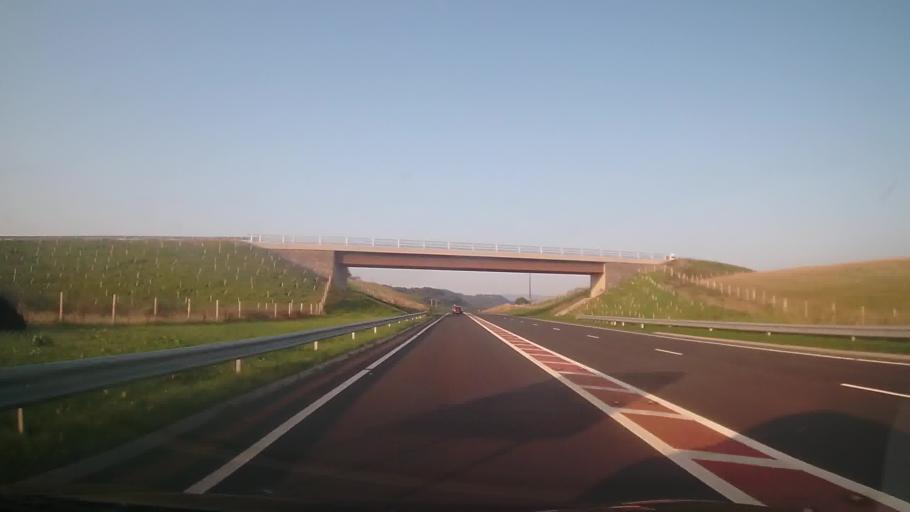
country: GB
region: Wales
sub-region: Sir Powys
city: Newtown
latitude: 52.5145
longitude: -3.2905
